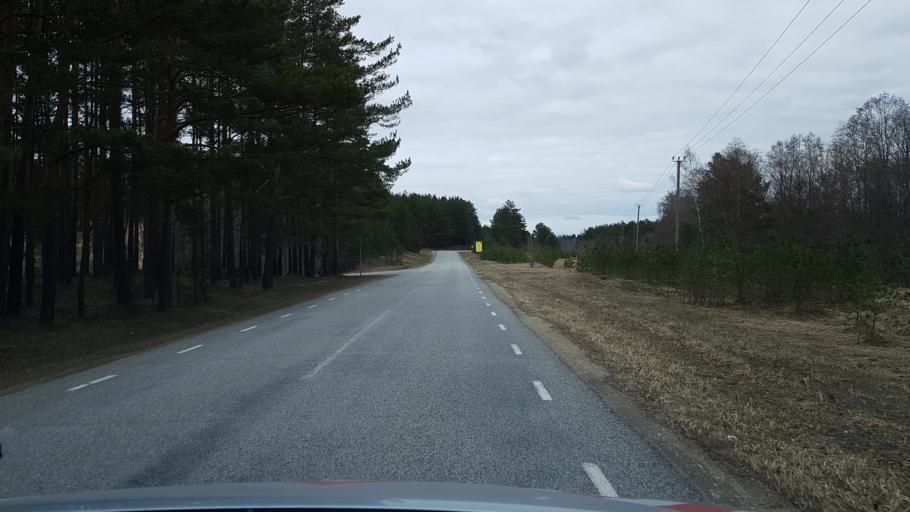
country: EE
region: Ida-Virumaa
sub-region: Narva linn
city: Narva
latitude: 59.4268
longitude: 28.1206
